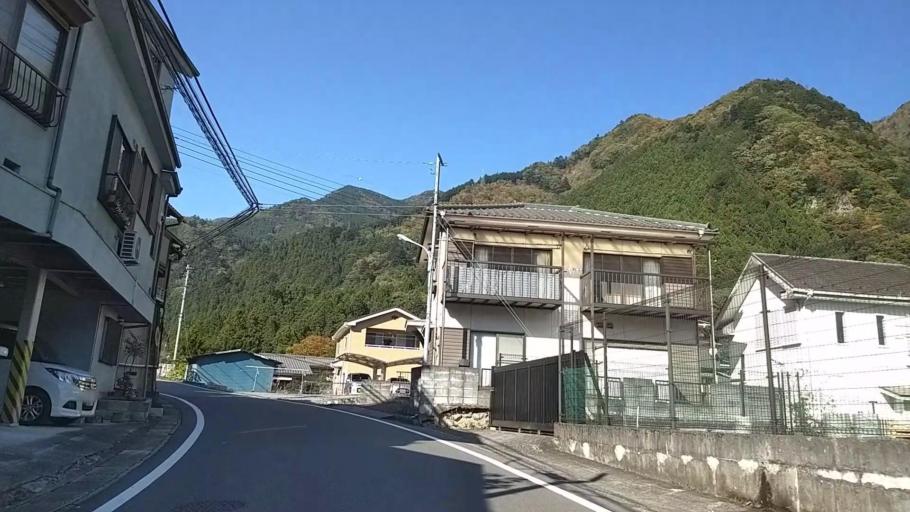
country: JP
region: Tokyo
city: Itsukaichi
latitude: 35.8115
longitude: 139.0951
